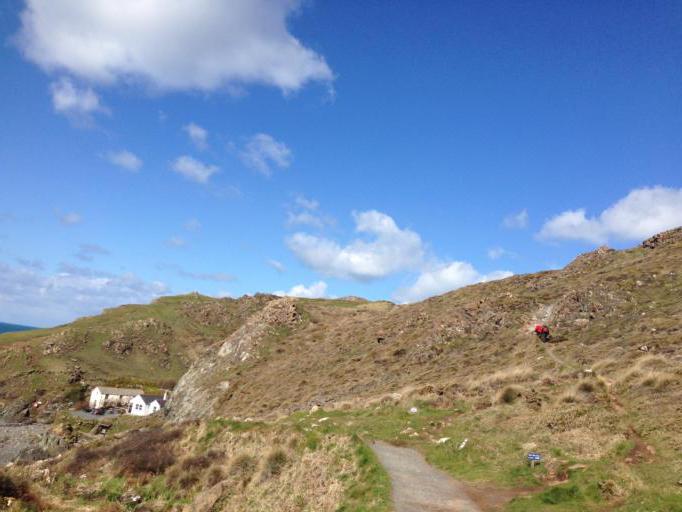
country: GB
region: England
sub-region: Cornwall
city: Landewednack
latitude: 49.9752
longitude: -5.2286
